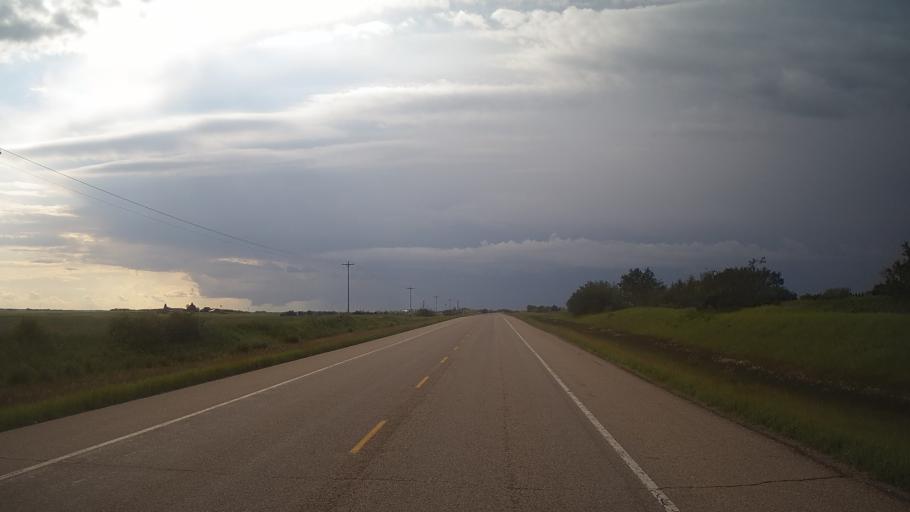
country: CA
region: Alberta
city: Vegreville
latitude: 53.2186
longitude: -112.1976
